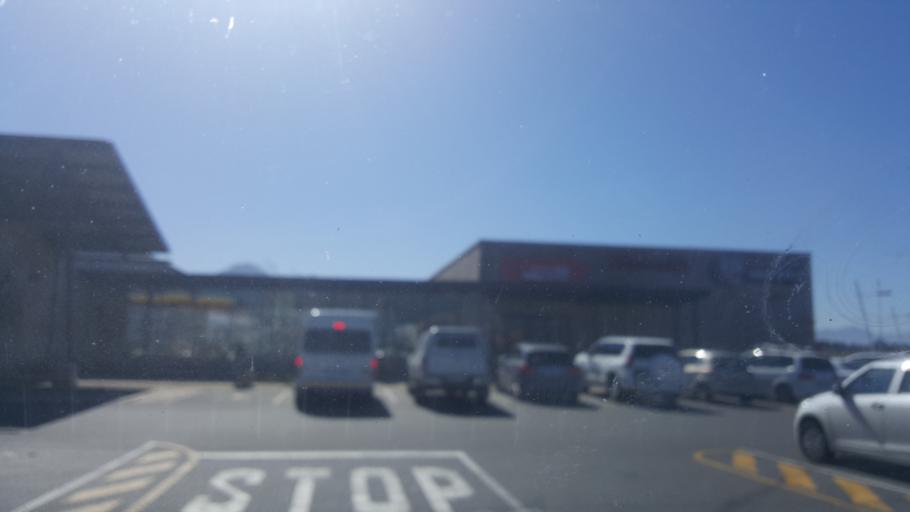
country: ZA
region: Western Cape
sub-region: Cape Winelands District Municipality
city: Worcester
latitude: -33.6337
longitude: 19.3588
